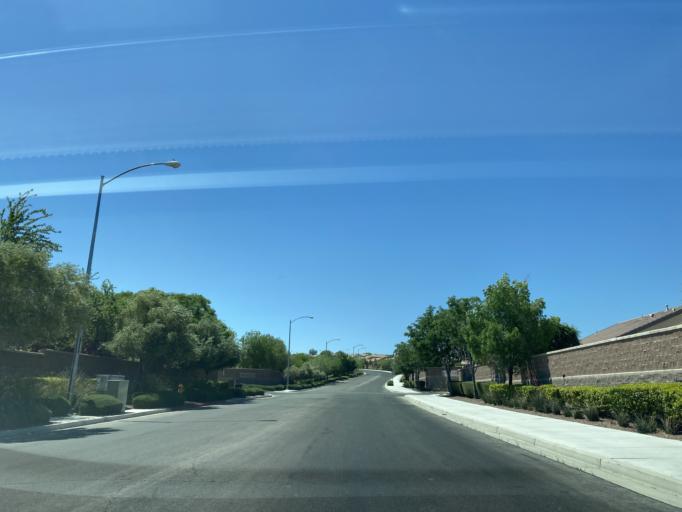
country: US
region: Nevada
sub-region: Clark County
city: Whitney
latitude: 35.9508
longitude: -115.0850
